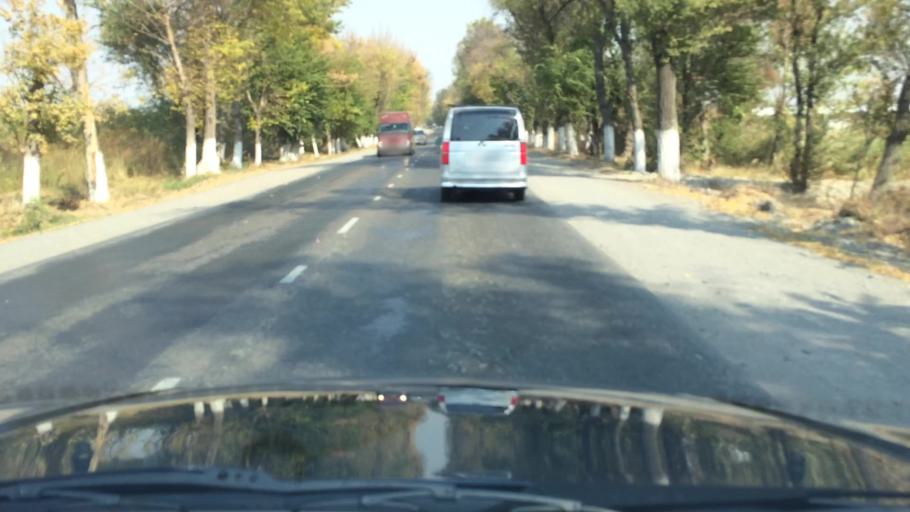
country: KG
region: Chuy
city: Lebedinovka
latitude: 42.9232
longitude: 74.6900
